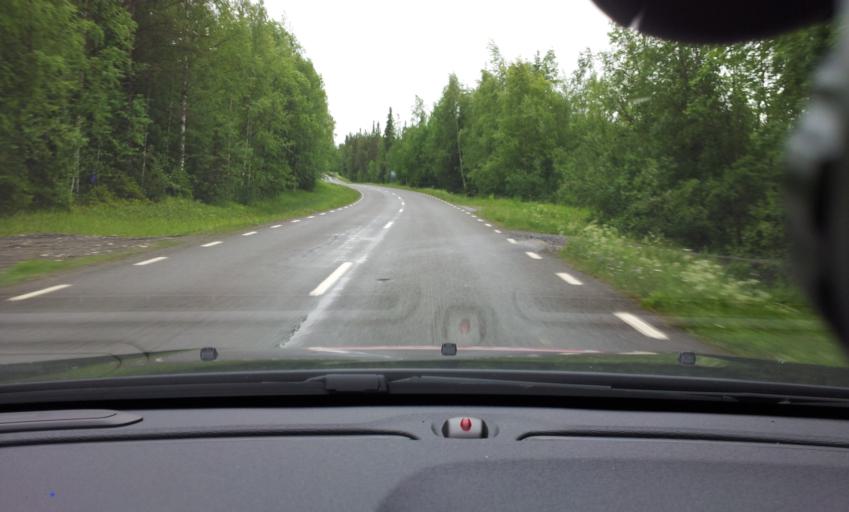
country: SE
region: Jaemtland
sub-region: Stroemsunds Kommun
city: Stroemsund
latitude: 63.4843
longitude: 15.4461
